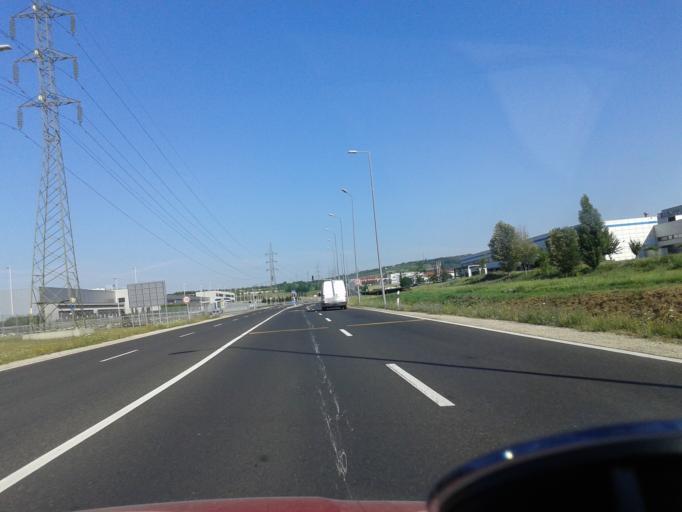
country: HU
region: Pest
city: Toeroekbalint
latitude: 47.4674
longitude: 18.8767
